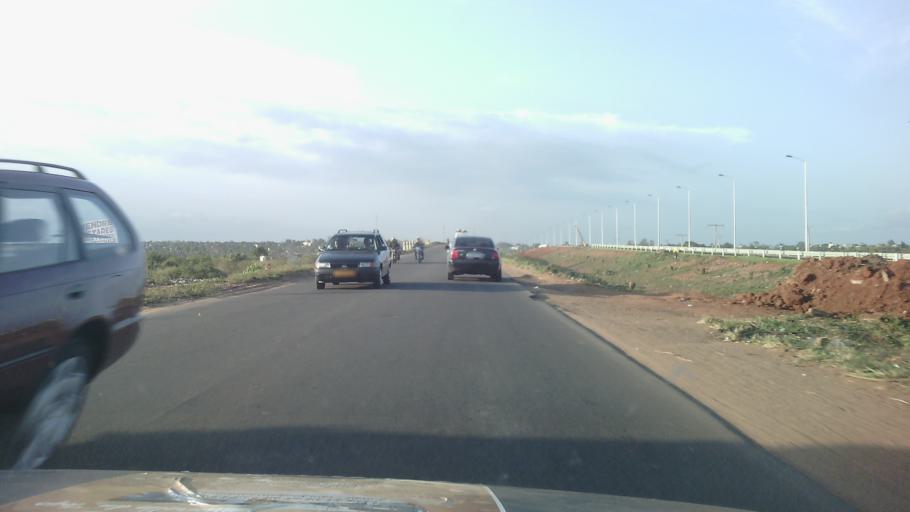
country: TG
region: Maritime
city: Tsevie
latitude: 6.3030
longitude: 1.2147
